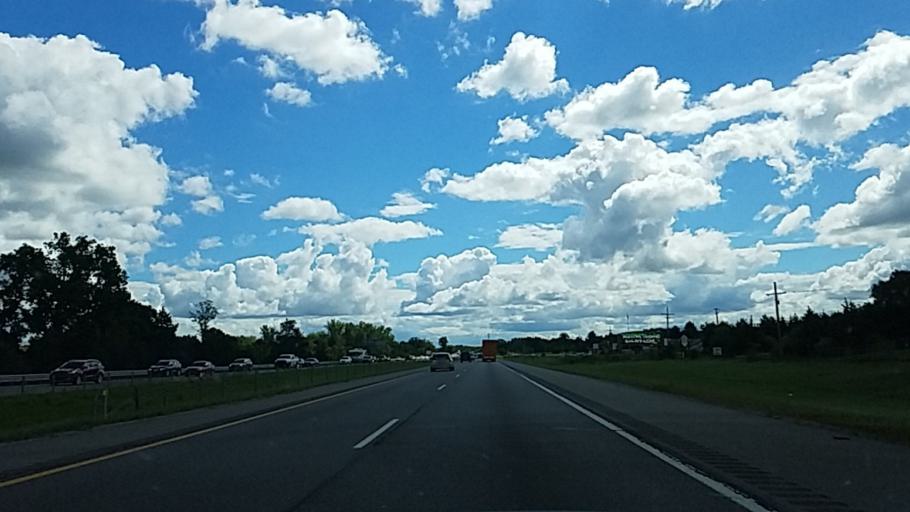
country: US
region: Michigan
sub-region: Livingston County
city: Brighton
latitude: 42.4951
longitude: -83.7577
